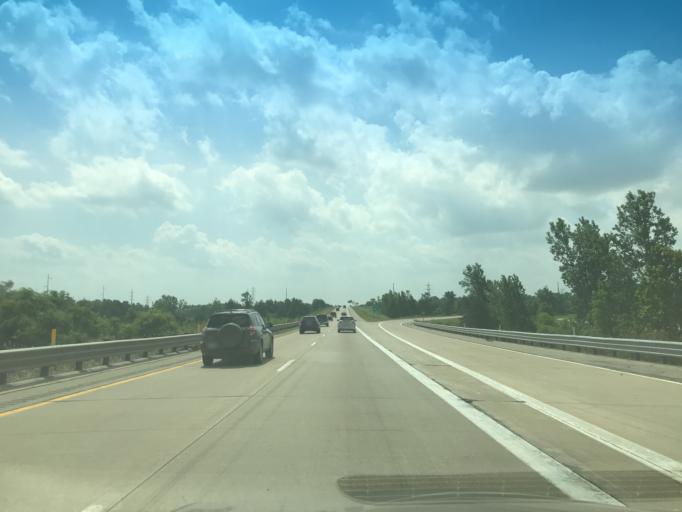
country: US
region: Michigan
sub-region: Eaton County
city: Dimondale
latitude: 42.6806
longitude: -84.6582
